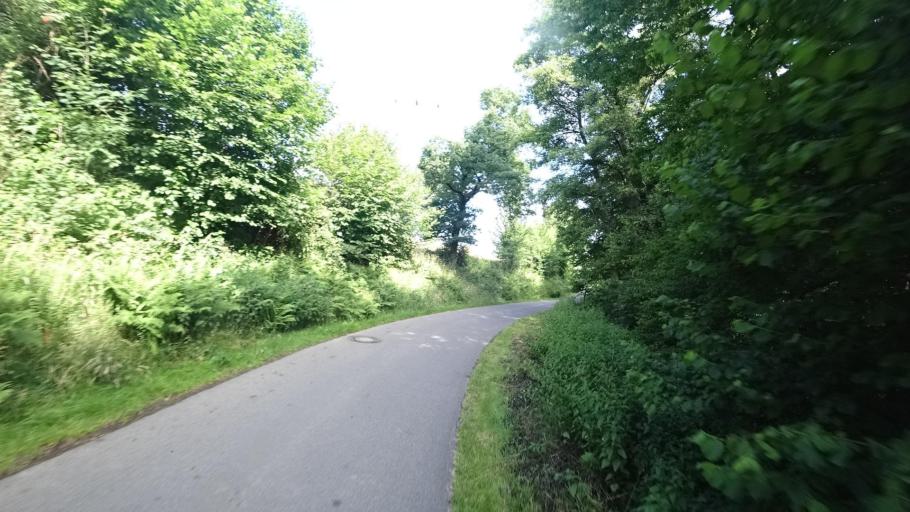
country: DE
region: Rheinland-Pfalz
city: Ratzert
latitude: 50.6502
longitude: 7.6196
